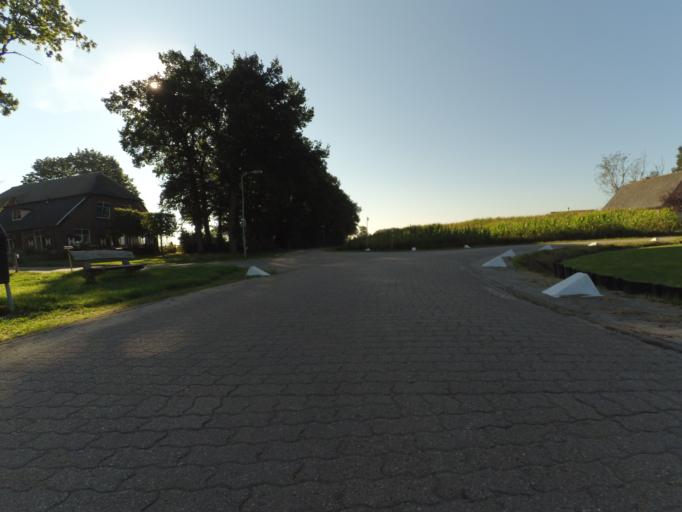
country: NL
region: Gelderland
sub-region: Gemeente Ermelo
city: Horst
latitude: 52.2874
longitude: 5.5778
